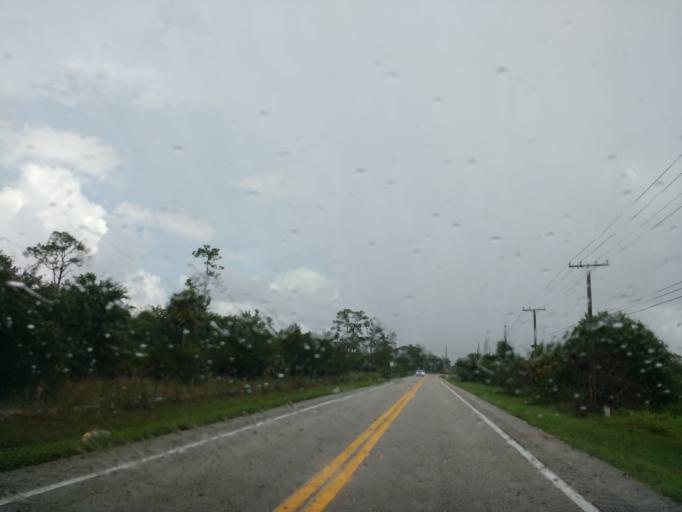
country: US
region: Florida
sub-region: Charlotte County
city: Charlotte Park
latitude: 26.8553
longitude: -82.0224
